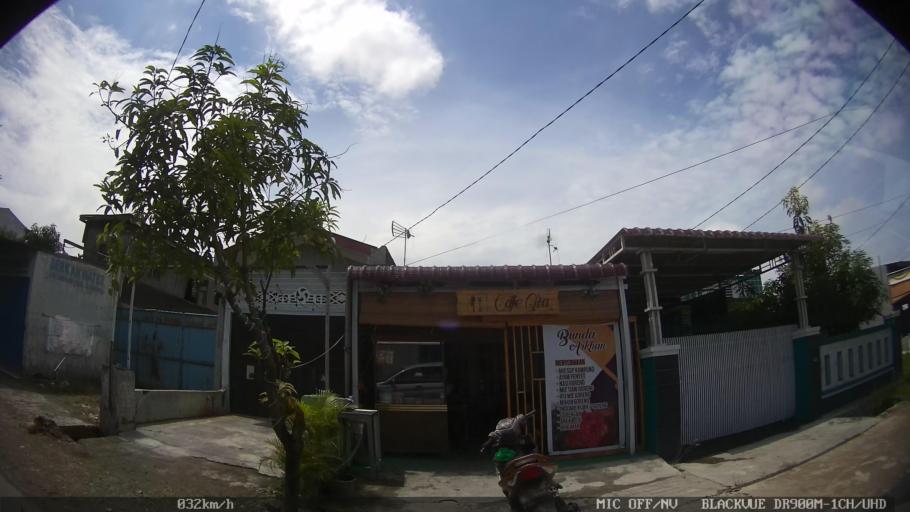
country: ID
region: North Sumatra
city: Percut
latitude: 3.6020
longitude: 98.7711
